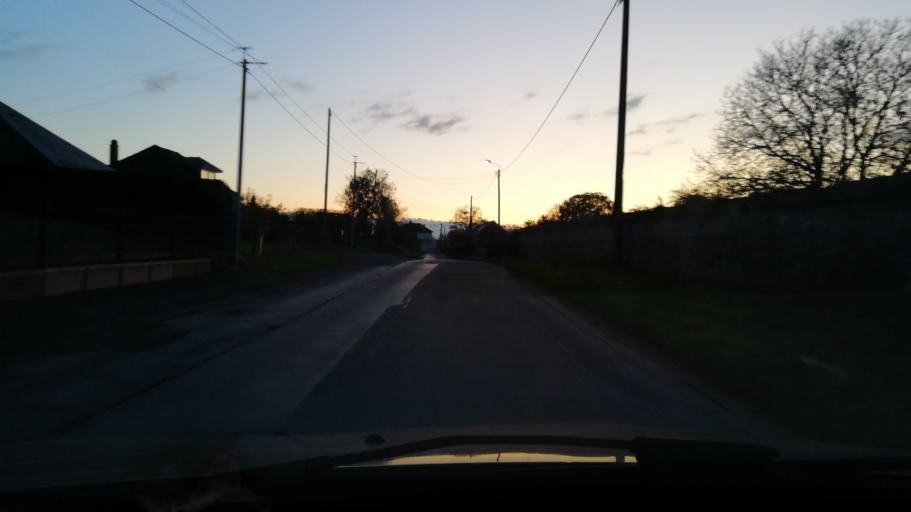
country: FR
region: Nord-Pas-de-Calais
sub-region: Departement du Nord
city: Marpent
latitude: 50.2652
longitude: 4.0873
